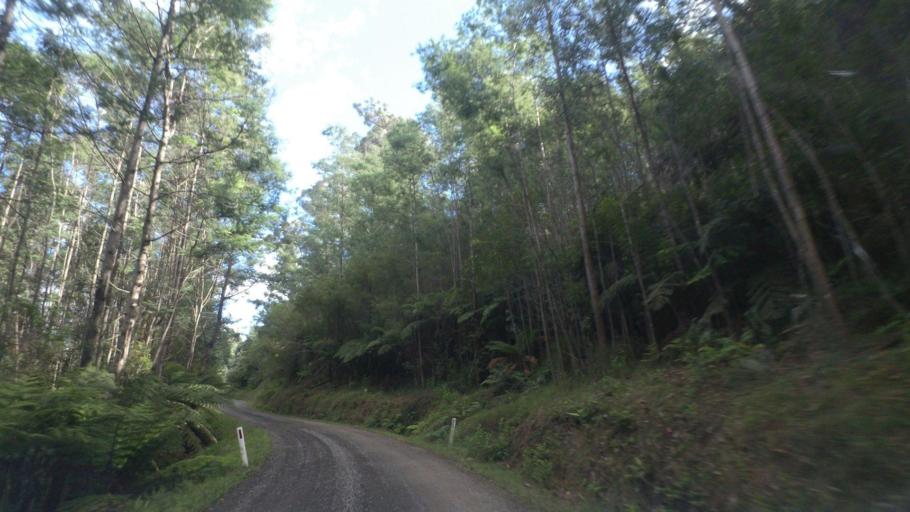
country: AU
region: Victoria
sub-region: Cardinia
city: Bunyip
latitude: -37.9739
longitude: 145.8230
